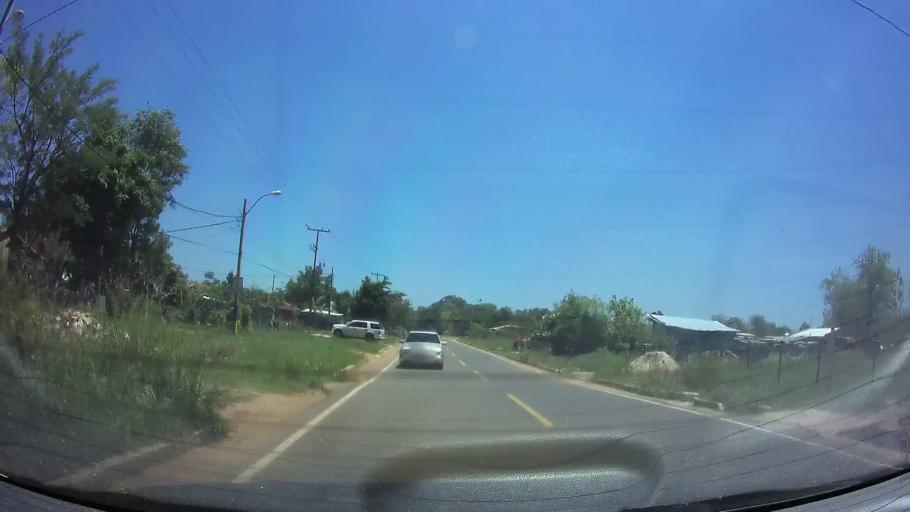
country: PY
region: Central
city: Limpio
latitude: -25.2426
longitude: -57.4911
